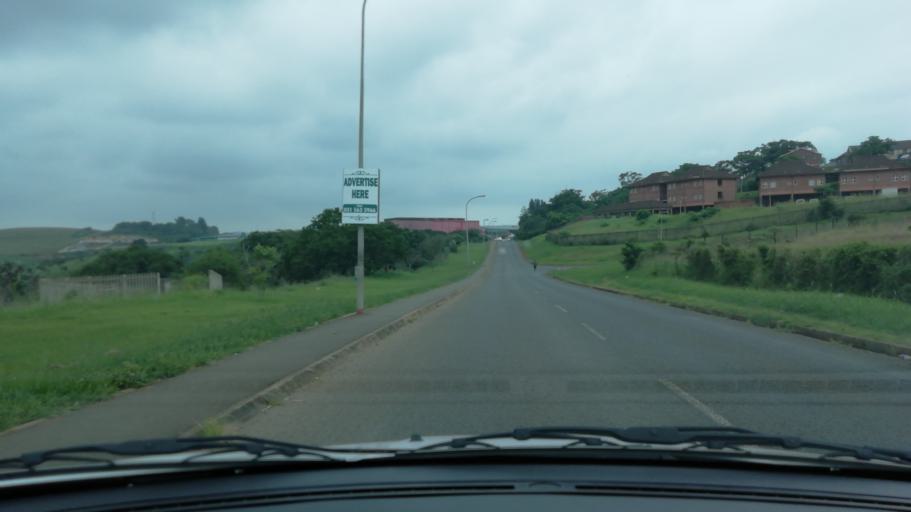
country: ZA
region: KwaZulu-Natal
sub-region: uThungulu District Municipality
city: Empangeni
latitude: -28.7483
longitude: 31.8854
